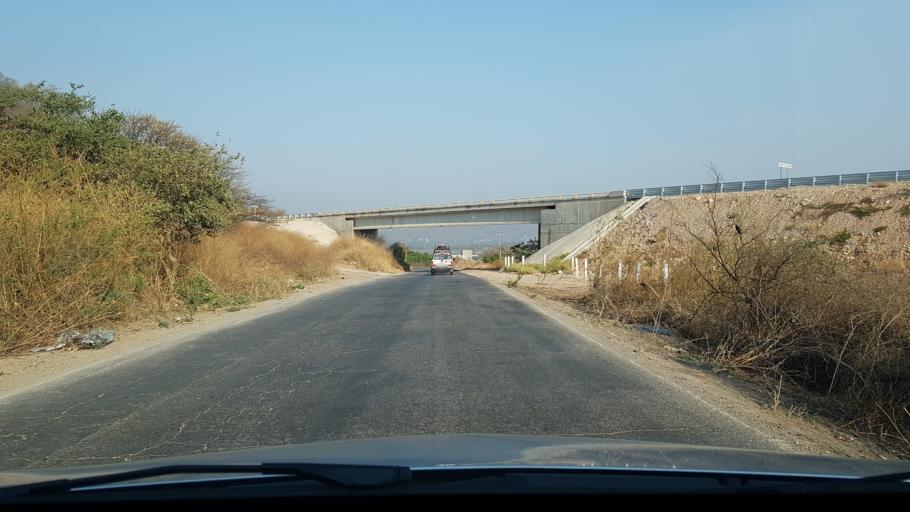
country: MX
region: Morelos
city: Tlaltizapan
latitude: 18.6780
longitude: -99.0800
